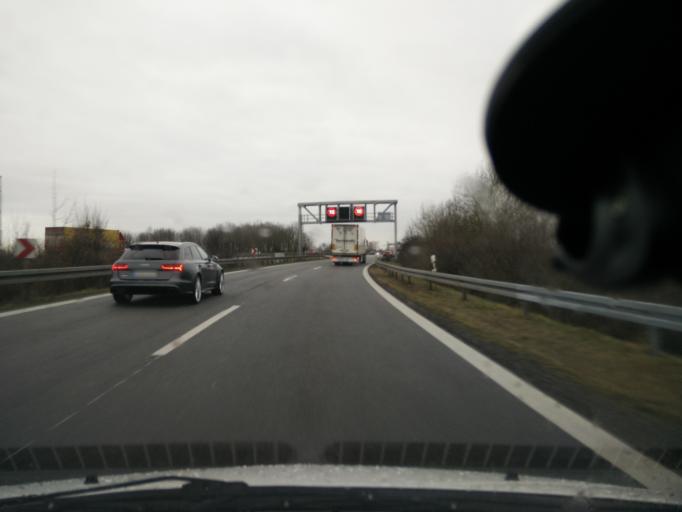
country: DE
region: Bavaria
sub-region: Upper Bavaria
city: Oberschleissheim
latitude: 48.2266
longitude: 11.5403
